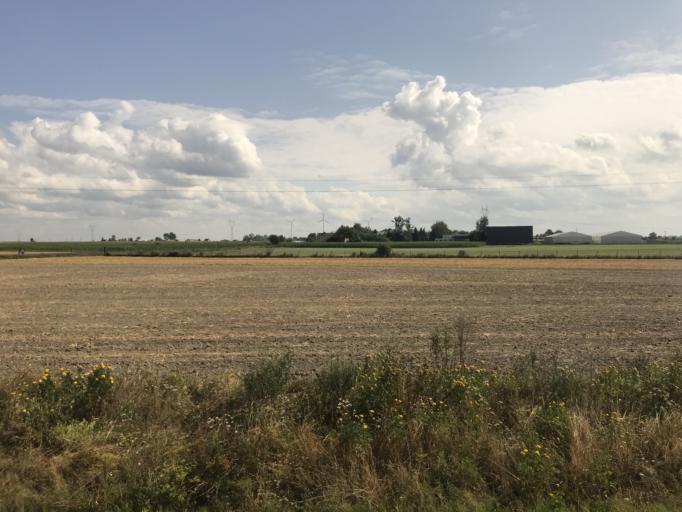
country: PL
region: Kujawsko-Pomorskie
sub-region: Powiat inowroclawski
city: Zlotniki Kujawskie
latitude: 52.9157
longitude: 18.1341
